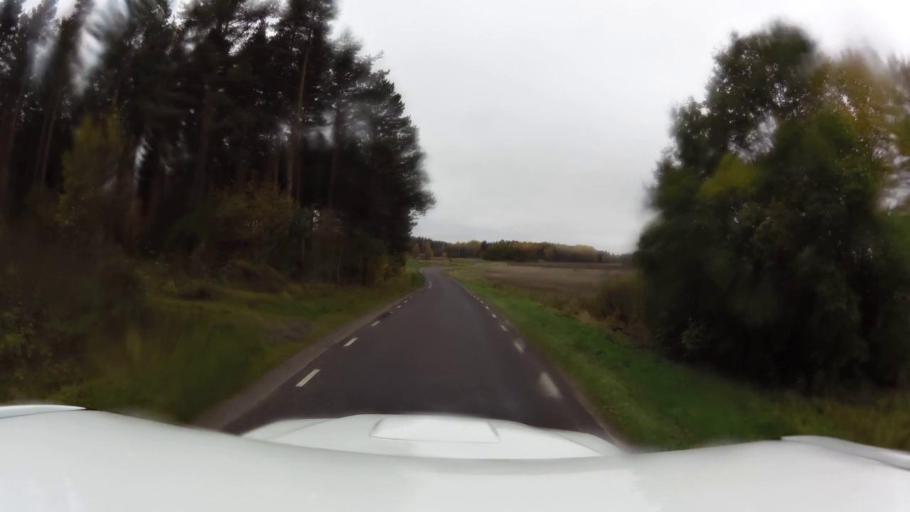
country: SE
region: OEstergoetland
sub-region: Linkopings Kommun
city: Linghem
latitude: 58.4653
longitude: 15.7834
